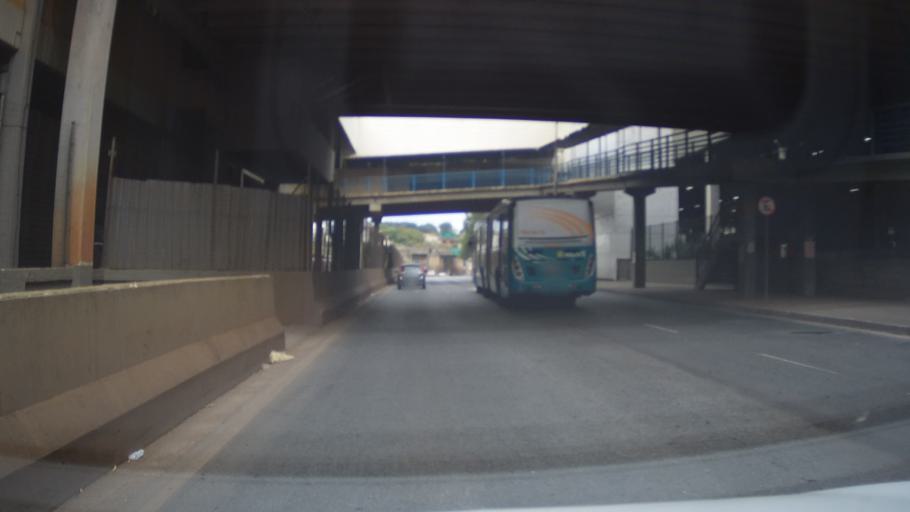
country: BR
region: Minas Gerais
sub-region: Belo Horizonte
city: Belo Horizonte
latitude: -19.8216
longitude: -43.9471
